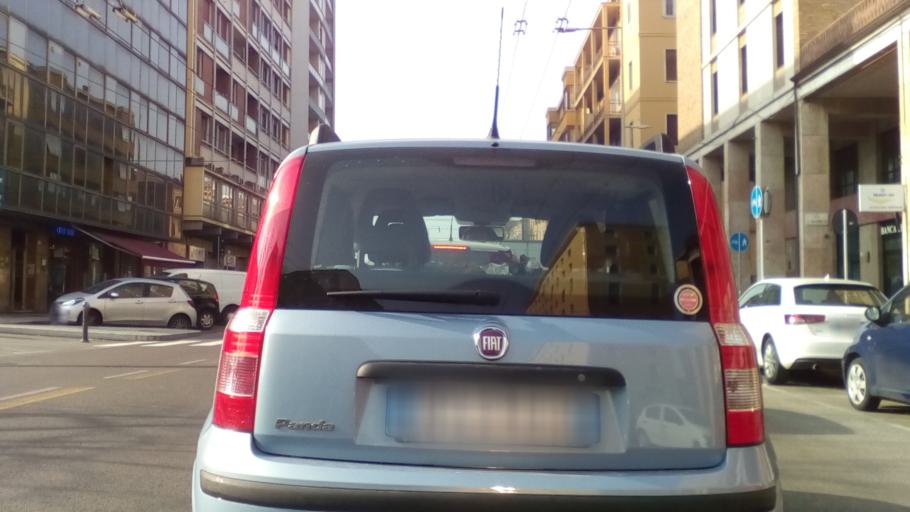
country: IT
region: Emilia-Romagna
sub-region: Provincia di Modena
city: Modena
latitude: 44.6427
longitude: 10.9350
